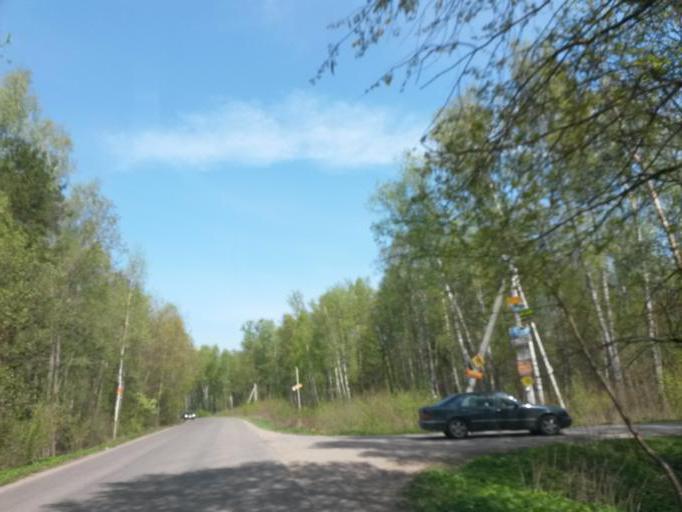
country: RU
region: Moskovskaya
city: Lyubuchany
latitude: 55.3128
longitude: 37.6160
